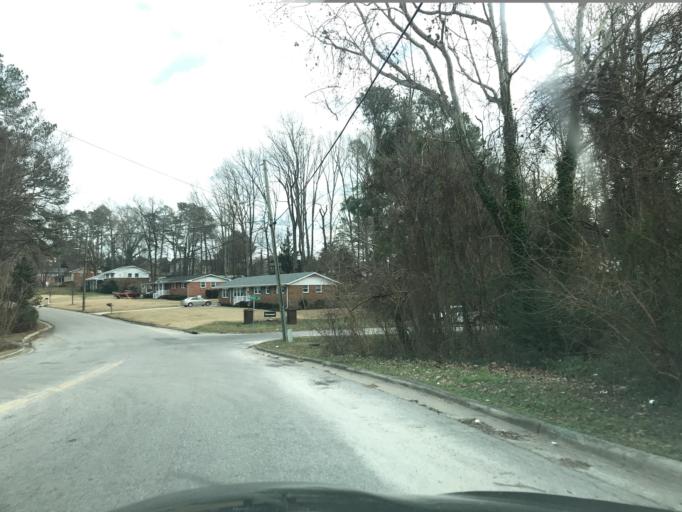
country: US
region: North Carolina
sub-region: Wake County
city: Raleigh
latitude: 35.8234
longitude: -78.5858
